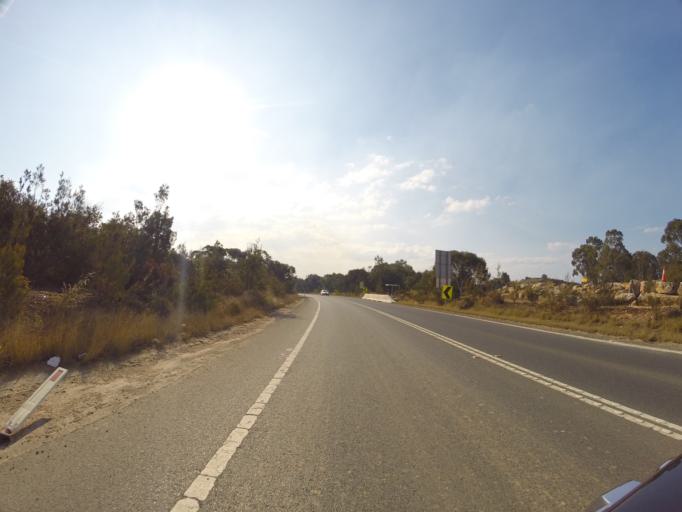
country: AU
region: New South Wales
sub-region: Liverpool
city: East Hills
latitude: -33.9929
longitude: 150.9967
